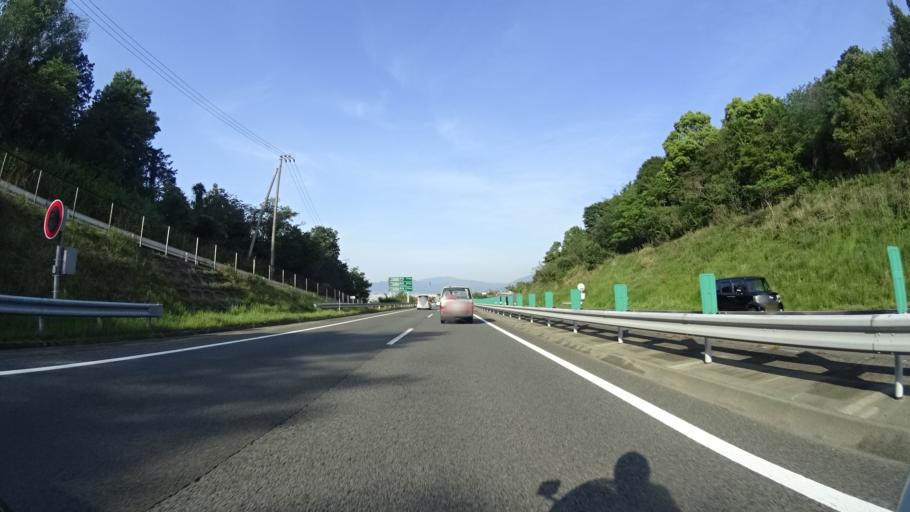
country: JP
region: Ehime
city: Kawanoecho
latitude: 33.9584
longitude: 133.4786
